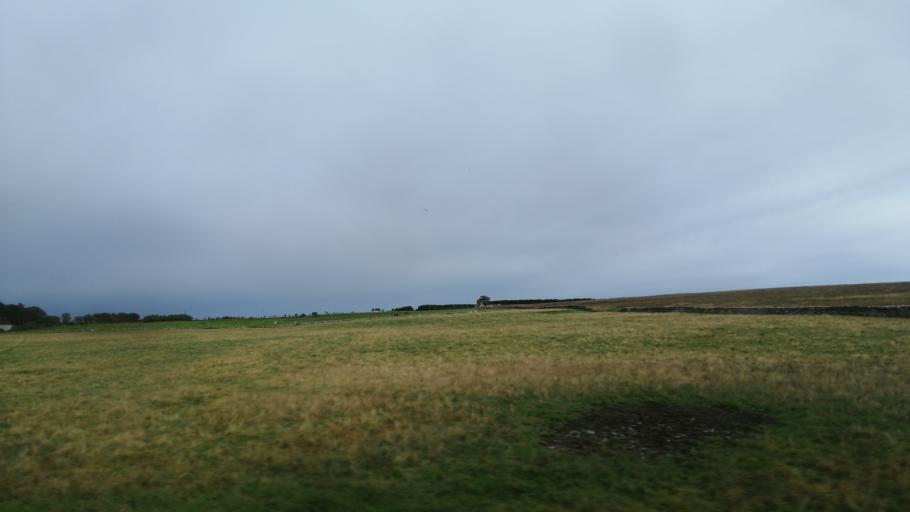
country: GB
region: Scotland
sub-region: Highland
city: Thurso
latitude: 58.4918
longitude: -3.5319
